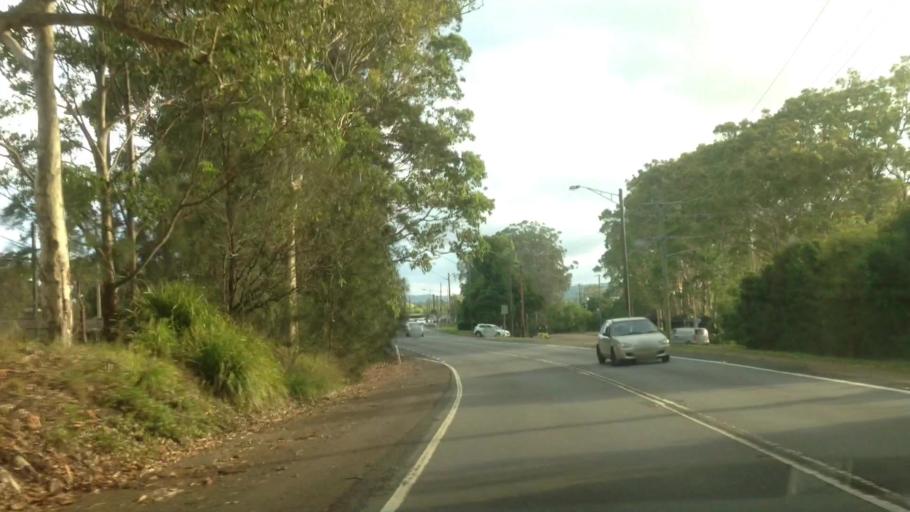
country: AU
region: New South Wales
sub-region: Wyong Shire
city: Chittaway Bay
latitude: -33.2882
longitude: 151.4242
